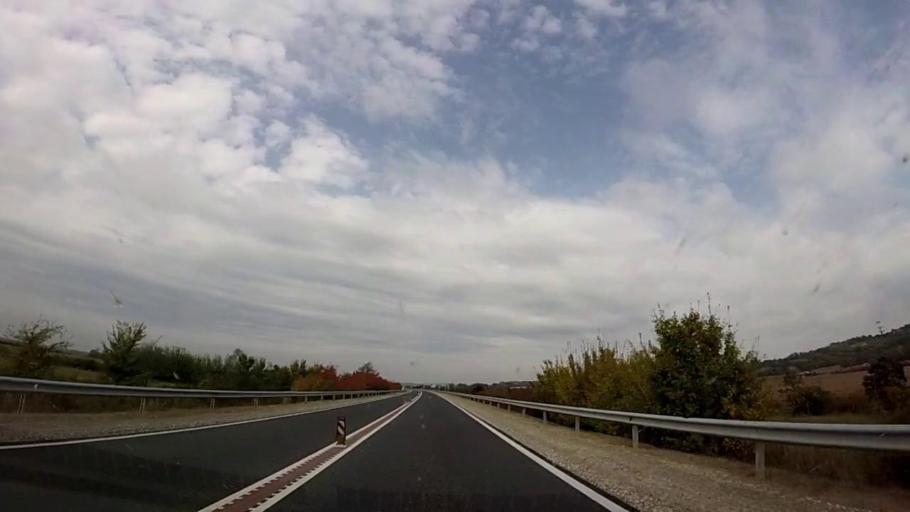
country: HR
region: Medimurska
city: Domasinec
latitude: 46.4974
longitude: 16.6239
